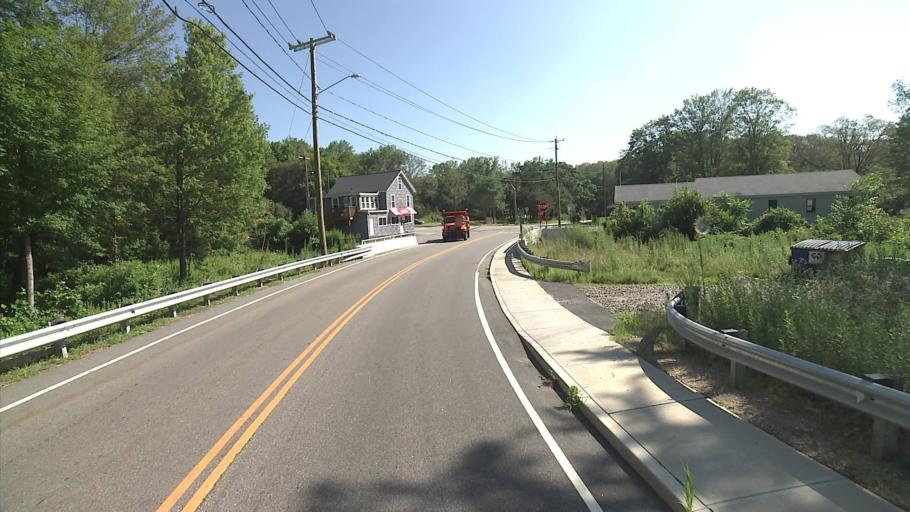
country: US
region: Connecticut
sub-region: New London County
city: Montville Center
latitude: 41.4657
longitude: -72.1586
